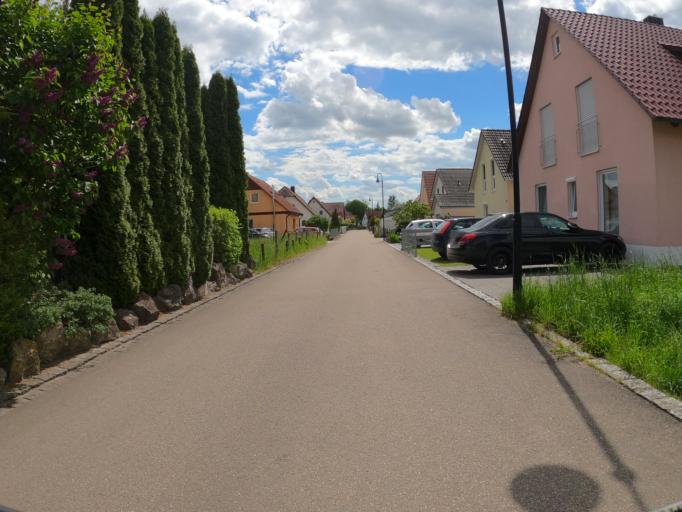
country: DE
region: Bavaria
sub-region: Swabia
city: Leipheim
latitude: 48.4587
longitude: 10.2145
